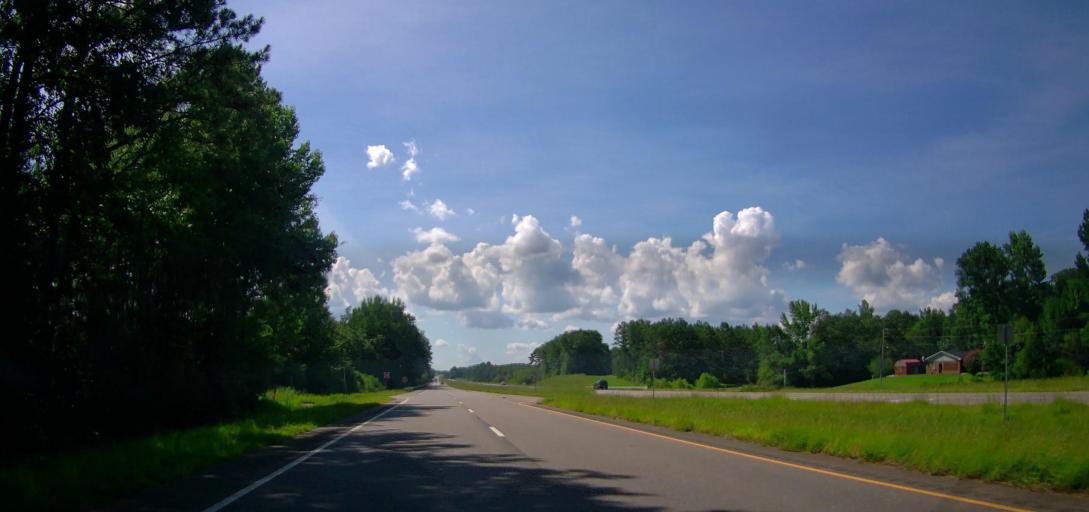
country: US
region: Alabama
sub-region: Pickens County
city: Gordo
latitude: 33.3423
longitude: -87.9428
